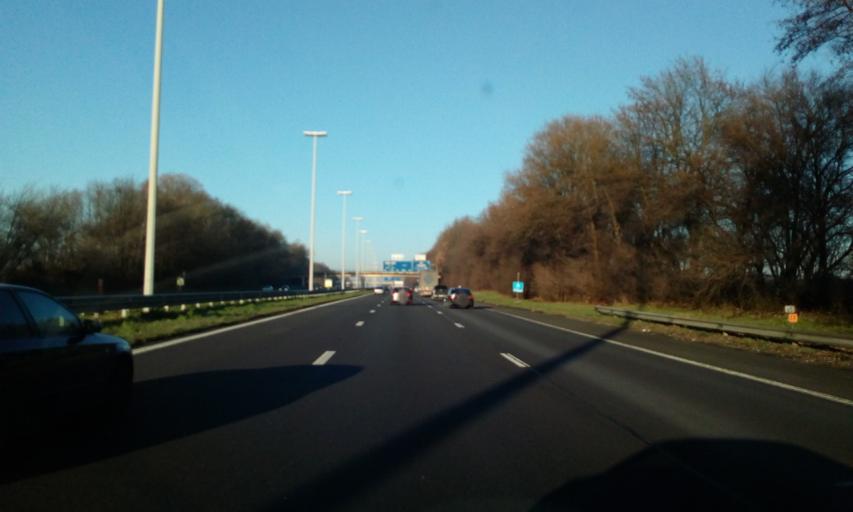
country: BE
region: Wallonia
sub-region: Province du Brabant Wallon
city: Braine-le-Chateau
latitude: 50.6520
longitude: 4.3096
